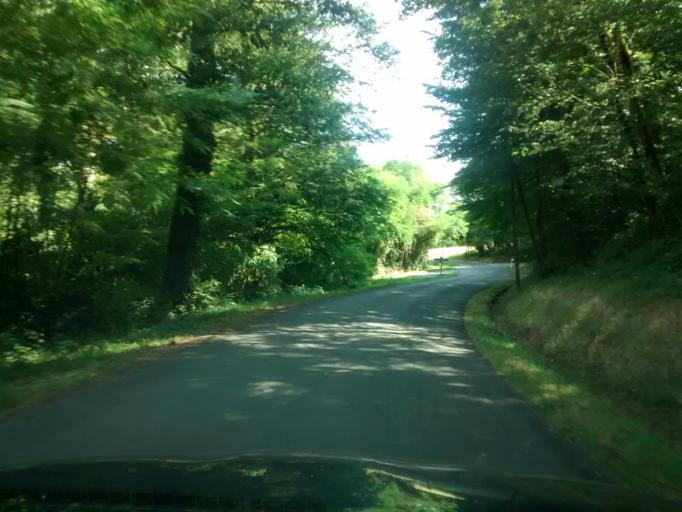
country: FR
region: Aquitaine
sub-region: Departement de la Dordogne
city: Saint-Cyprien
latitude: 44.8239
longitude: 1.0701
